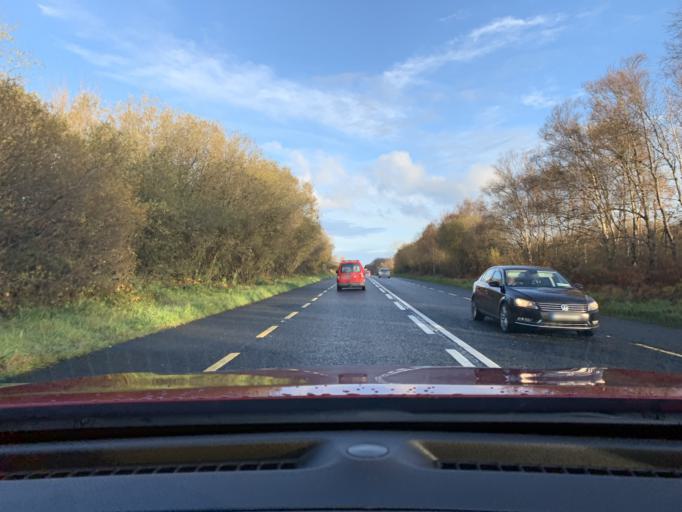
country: IE
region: Connaught
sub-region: Sligo
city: Sligo
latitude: 54.3762
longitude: -8.5289
